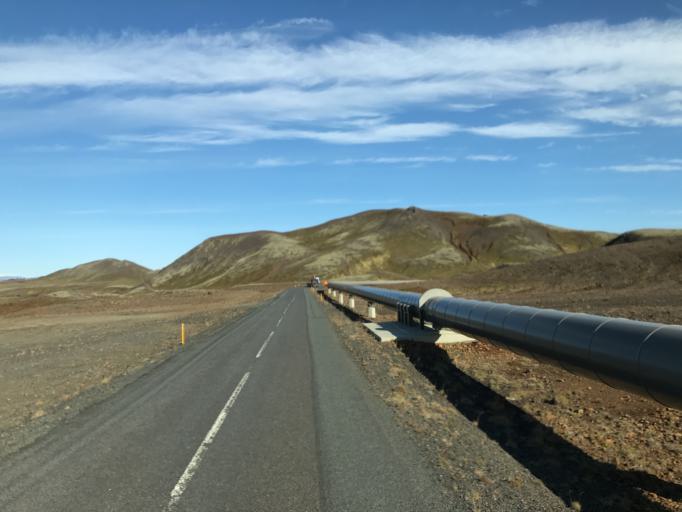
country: IS
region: South
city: Hveragerdi
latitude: 64.1233
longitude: -21.3123
